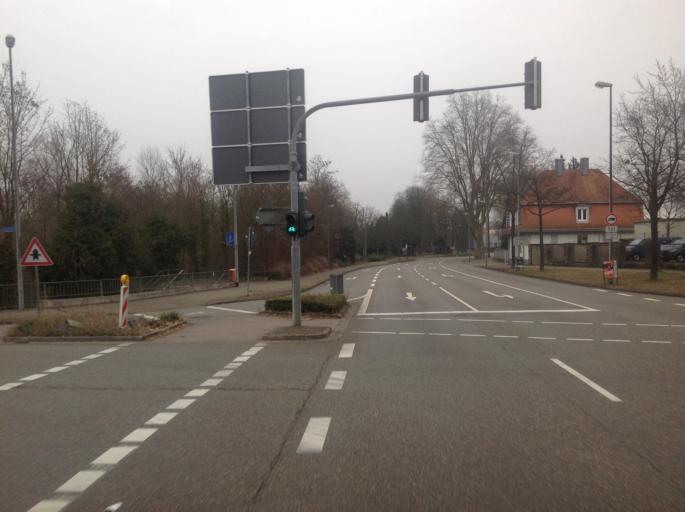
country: DE
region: Baden-Wuerttemberg
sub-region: Karlsruhe Region
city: Rastatt
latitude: 48.8465
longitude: 8.2004
